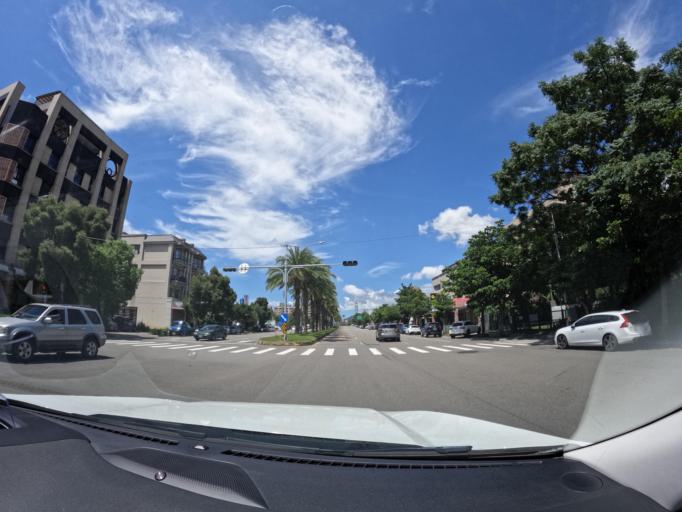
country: TW
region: Taipei
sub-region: Taipei
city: Banqiao
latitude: 25.0822
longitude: 121.3839
